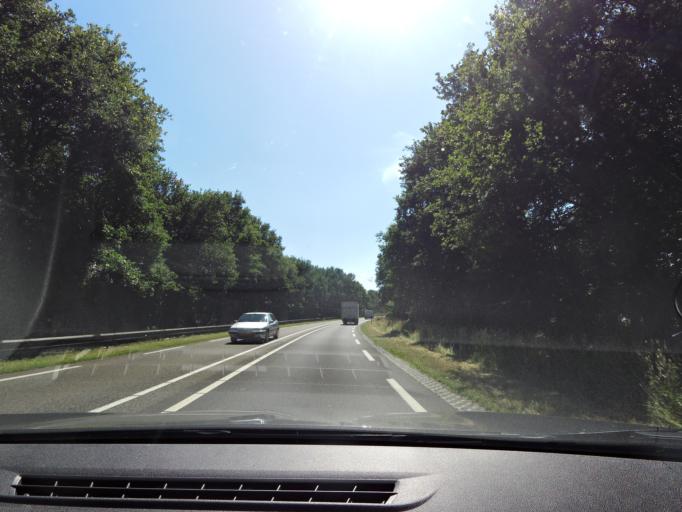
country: NL
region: Gelderland
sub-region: Berkelland
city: Eibergen
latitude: 52.0364
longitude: 6.6283
